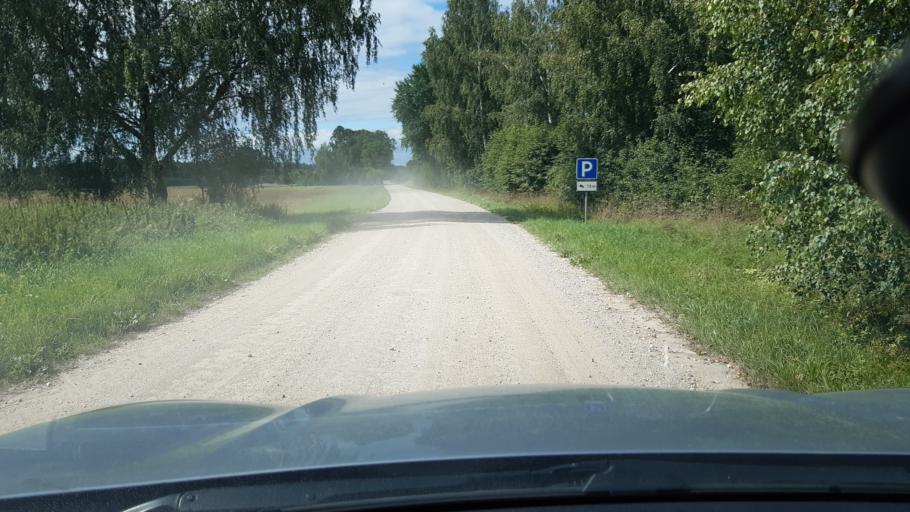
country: EE
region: Paernumaa
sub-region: Vaendra vald (alev)
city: Vandra
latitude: 58.7943
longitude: 24.9984
